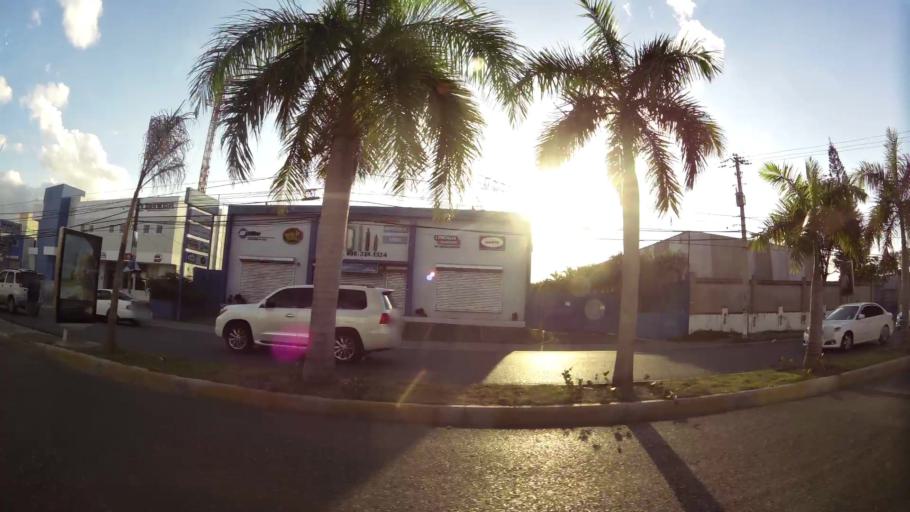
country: DO
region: Santiago
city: Santiago de los Caballeros
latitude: 19.4825
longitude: -70.7188
